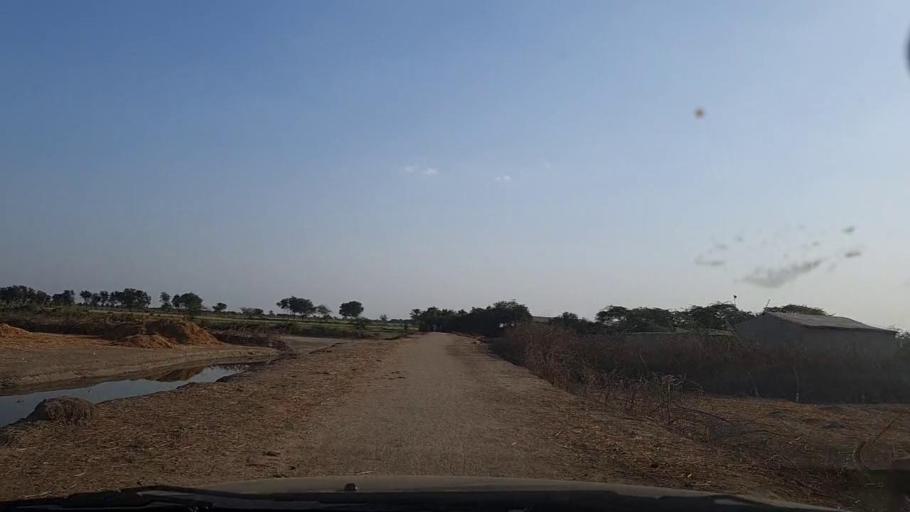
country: PK
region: Sindh
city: Daro Mehar
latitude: 24.7470
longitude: 68.0944
